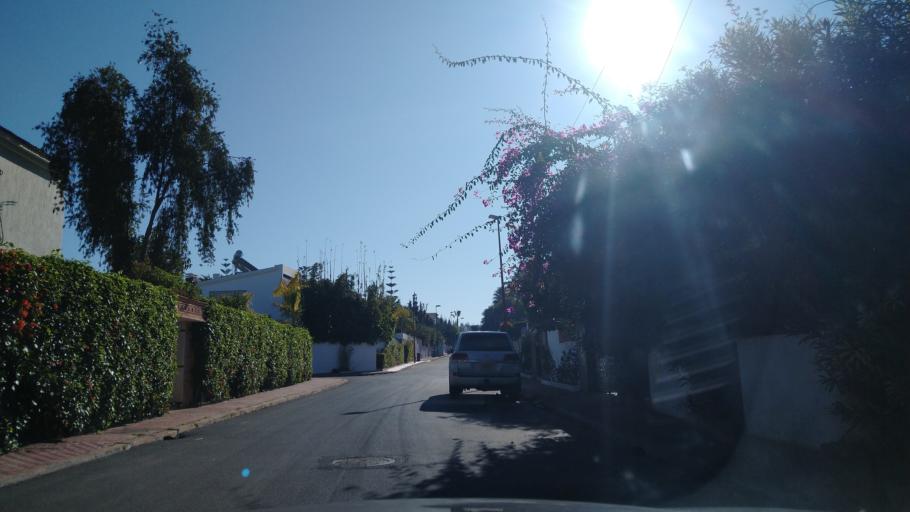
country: MA
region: Rabat-Sale-Zemmour-Zaer
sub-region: Skhirate-Temara
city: Temara
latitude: 33.9607
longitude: -6.8623
